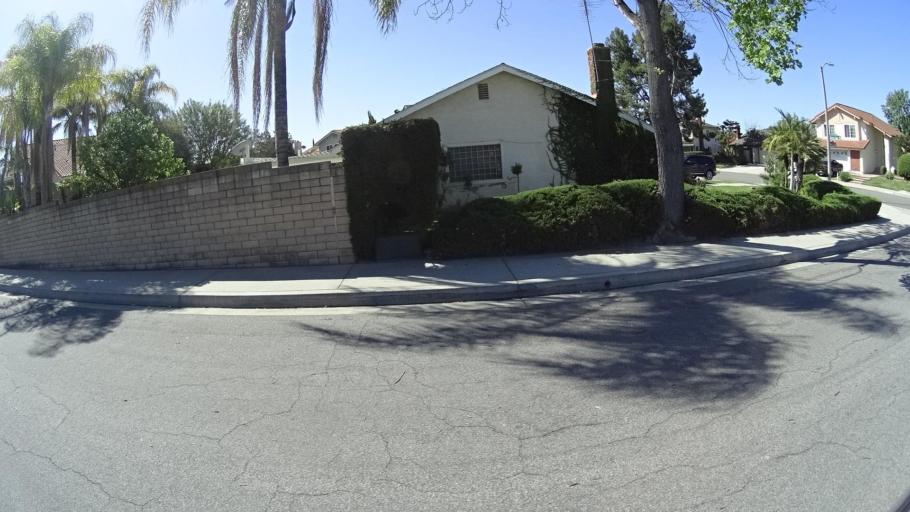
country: US
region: California
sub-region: Los Angeles County
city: Diamond Bar
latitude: 33.9993
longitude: -117.8242
